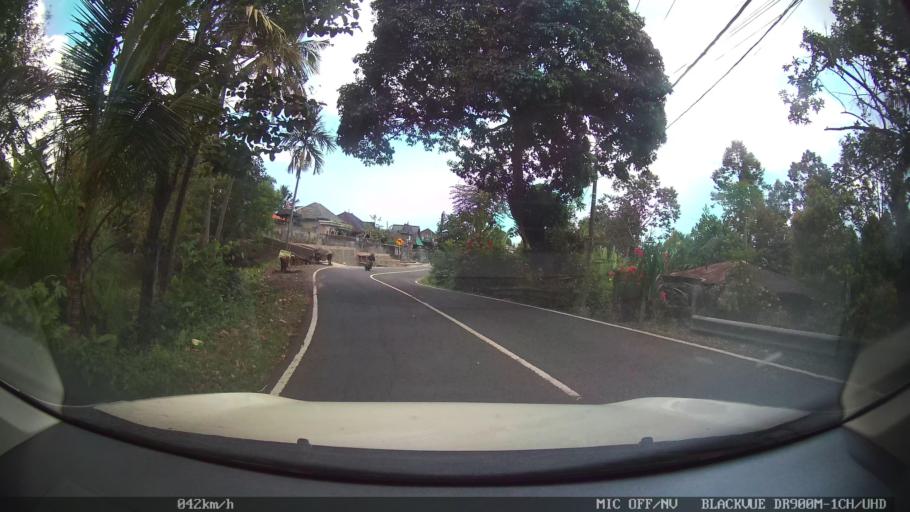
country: ID
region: Bali
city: Banjar Ambengan
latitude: -8.1781
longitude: 115.1307
